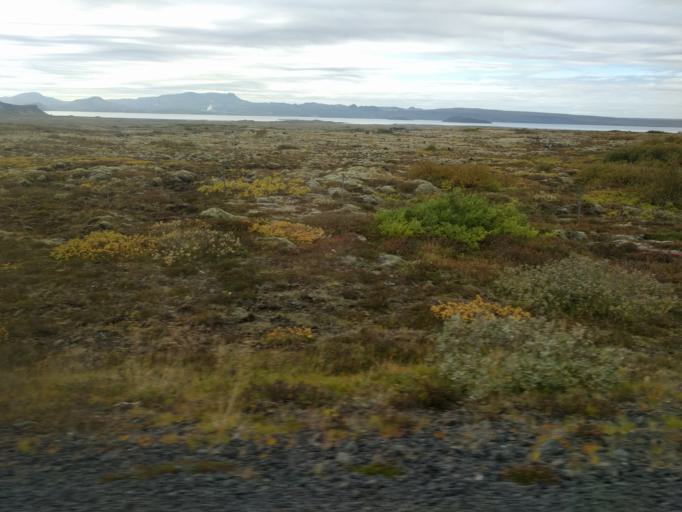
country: IS
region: South
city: Hveragerdi
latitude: 64.2013
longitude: -21.0345
